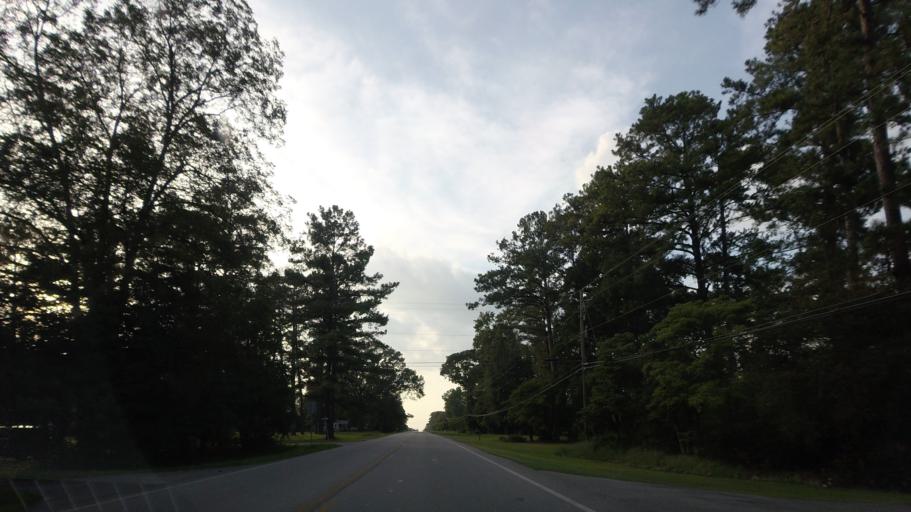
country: US
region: Georgia
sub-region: Wilkinson County
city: Gordon
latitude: 32.8863
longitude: -83.3473
